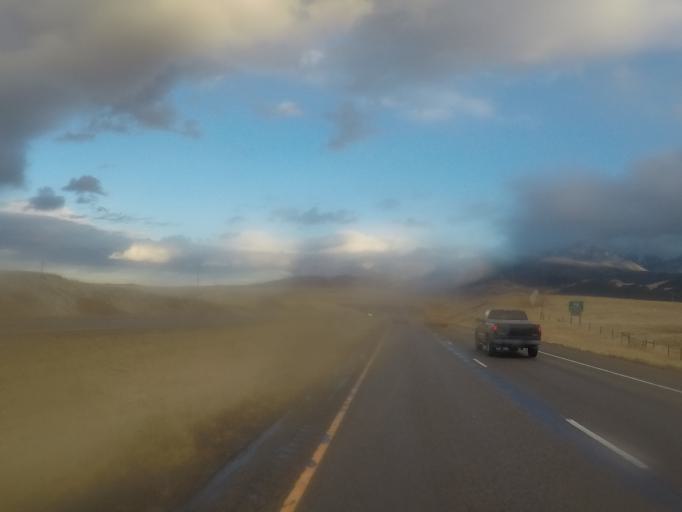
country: US
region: Montana
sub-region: Park County
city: Livingston
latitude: 45.6469
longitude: -110.5964
